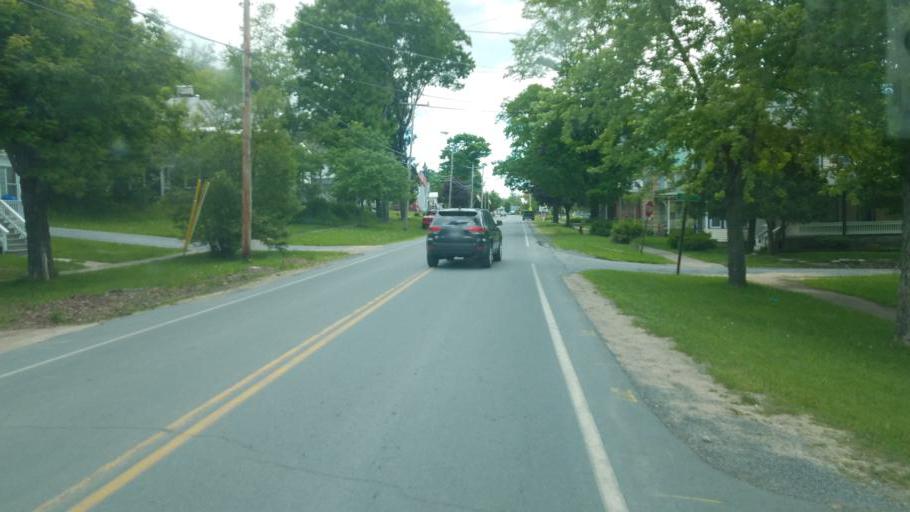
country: US
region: New York
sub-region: Oneida County
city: Boonville
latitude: 43.3295
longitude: -75.1873
